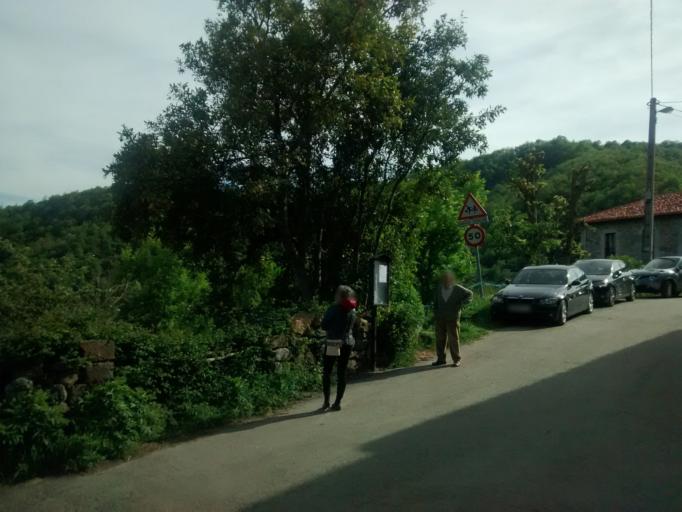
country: ES
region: Cantabria
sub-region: Provincia de Cantabria
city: Potes
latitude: 43.1931
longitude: -4.6344
